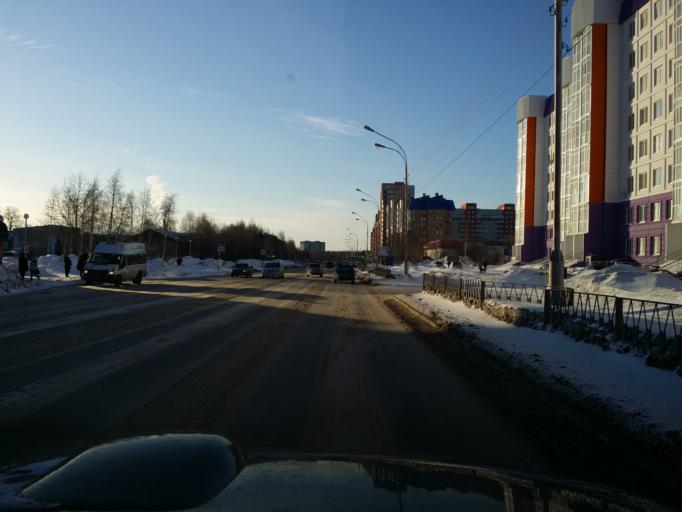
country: RU
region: Khanty-Mansiyskiy Avtonomnyy Okrug
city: Nizhnevartovsk
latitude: 60.9284
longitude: 76.5810
